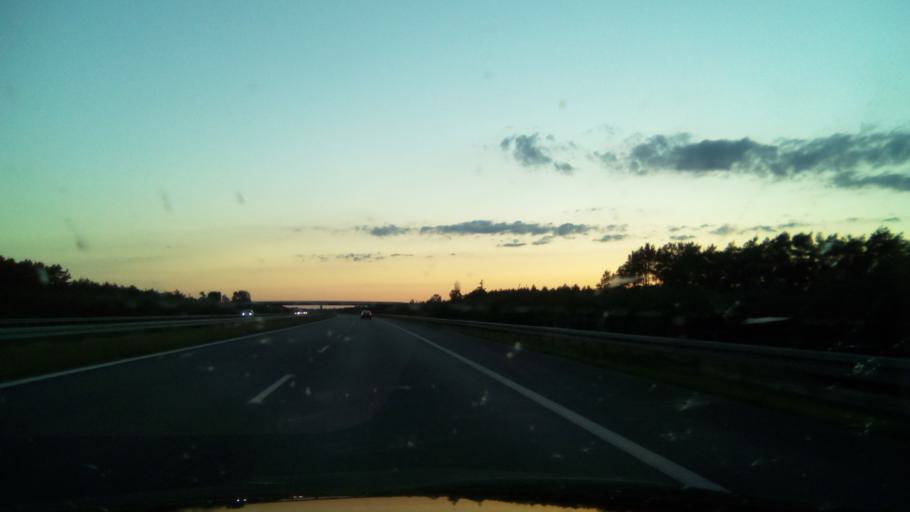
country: PL
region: Greater Poland Voivodeship
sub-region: Powiat kolski
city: Grzegorzew
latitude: 52.1182
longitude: 18.7195
